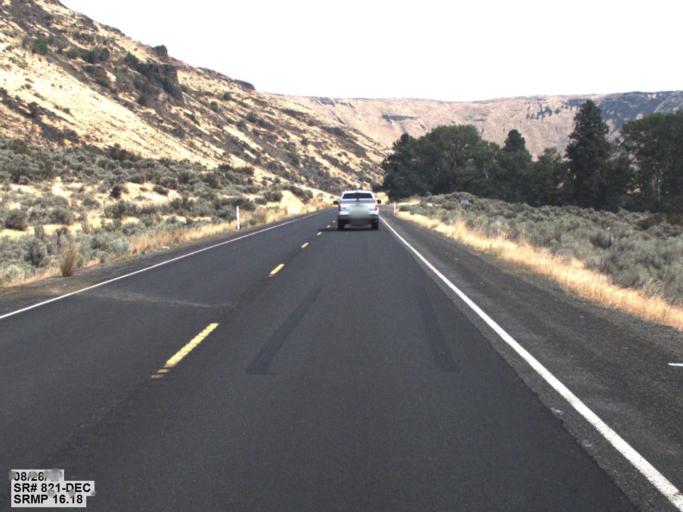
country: US
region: Washington
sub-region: Kittitas County
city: Kittitas
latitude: 46.8547
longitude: -120.4776
